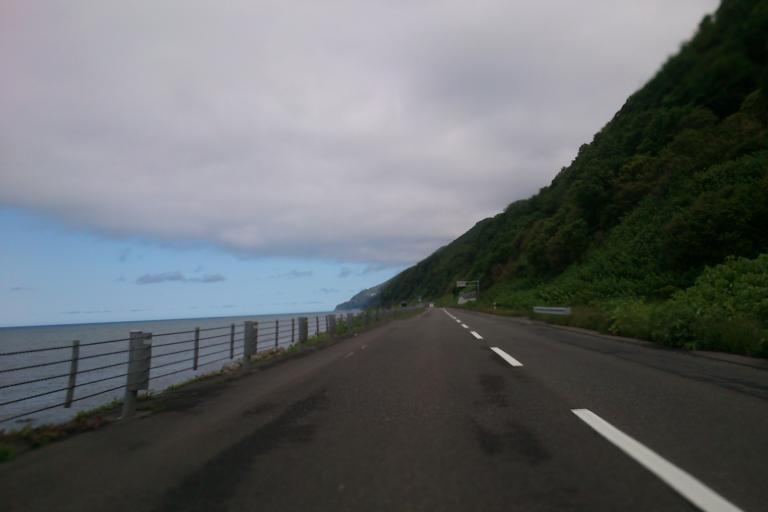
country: JP
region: Hokkaido
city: Ishikari
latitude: 43.4291
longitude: 141.4214
